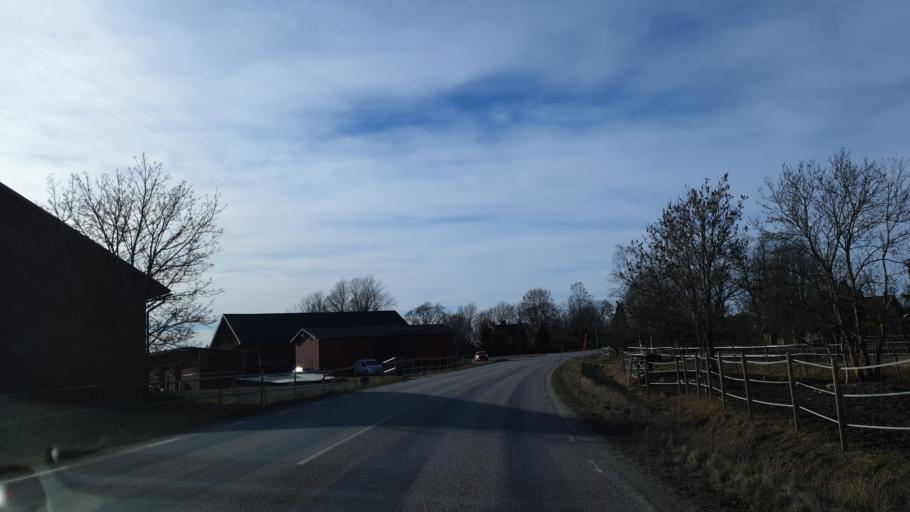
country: SE
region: Uppsala
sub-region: Enkopings Kommun
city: Grillby
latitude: 59.5943
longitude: 17.1805
